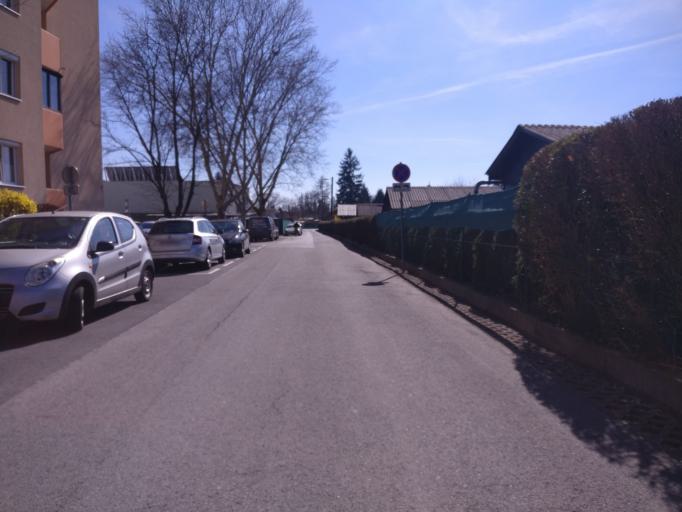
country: AT
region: Styria
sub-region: Graz Stadt
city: Wetzelsdorf
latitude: 47.0554
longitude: 15.4226
